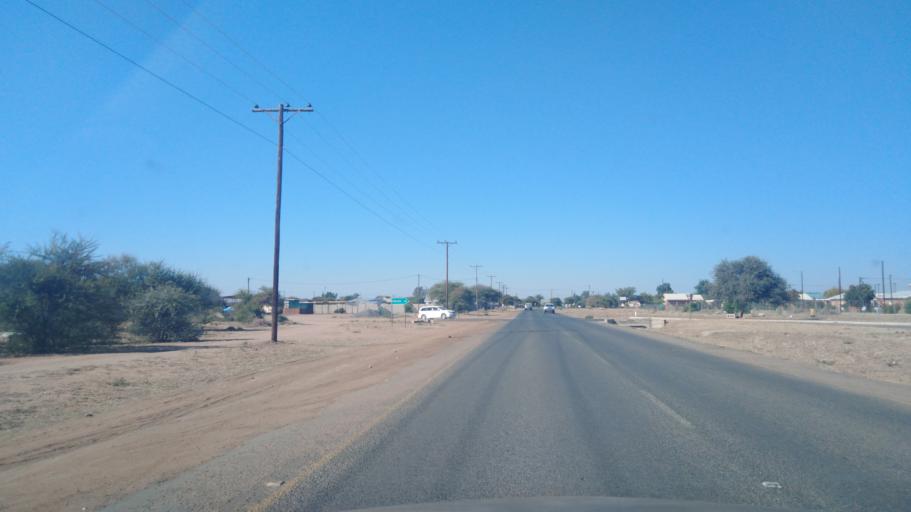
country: BW
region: Central
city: Mahalapye
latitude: -23.1216
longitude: 26.7950
